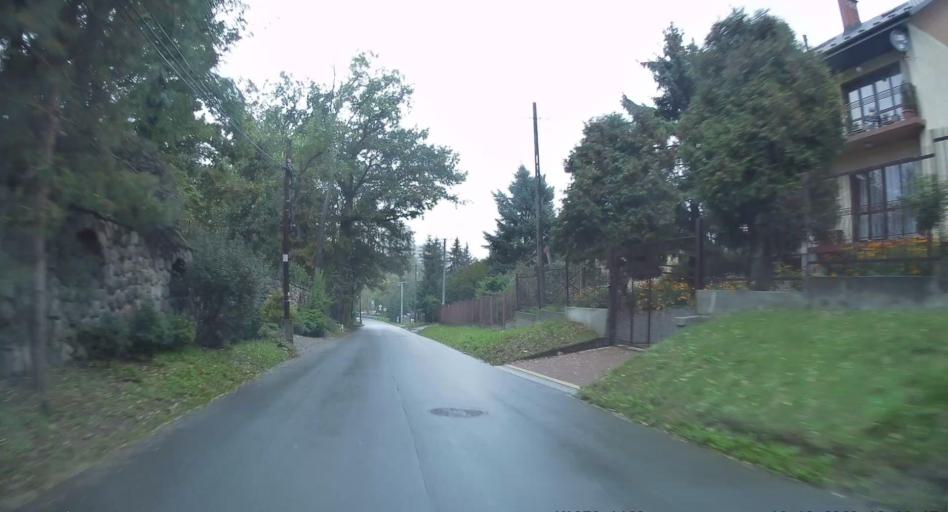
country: PL
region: Lesser Poland Voivodeship
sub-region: Powiat krakowski
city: Ochojno
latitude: 50.0092
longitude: 19.9810
